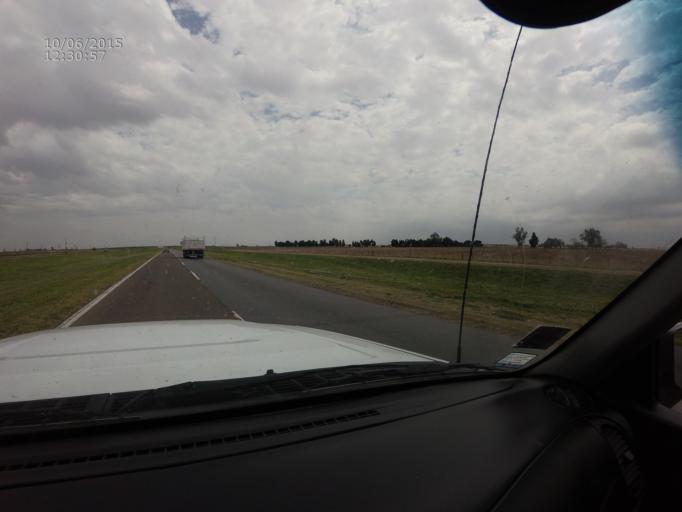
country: AR
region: Santa Fe
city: Carcarana
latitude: -32.8864
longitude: -61.1135
